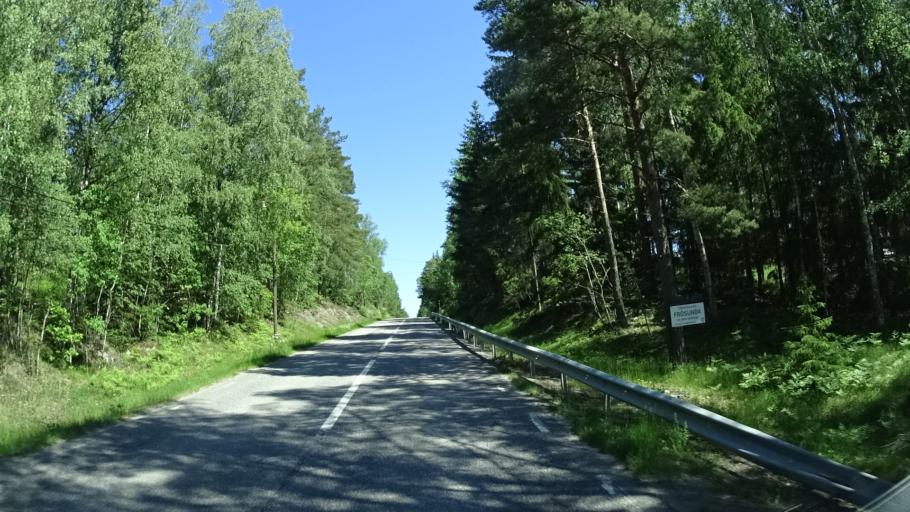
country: SE
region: Stockholm
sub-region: Vallentuna Kommun
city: Vallentuna
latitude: 59.6058
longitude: 18.1415
